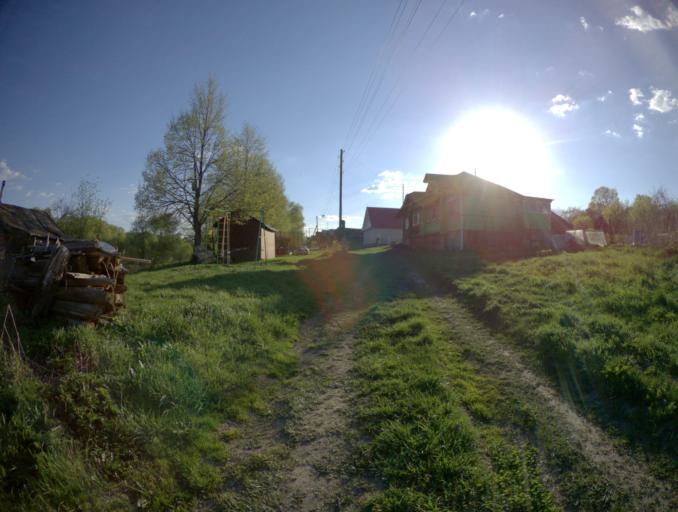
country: RU
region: Ivanovo
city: Gavrilov Posad
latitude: 56.3819
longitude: 40.1373
